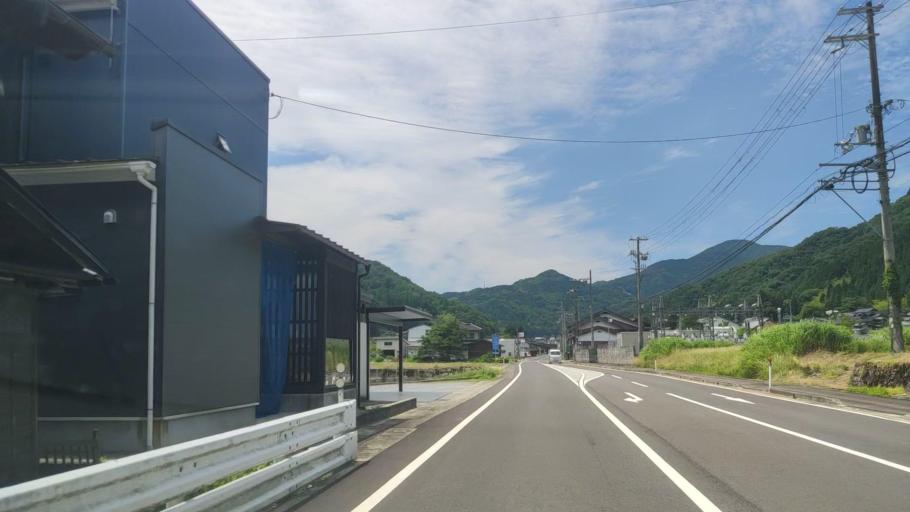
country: JP
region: Hyogo
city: Toyooka
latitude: 35.4662
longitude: 134.5467
